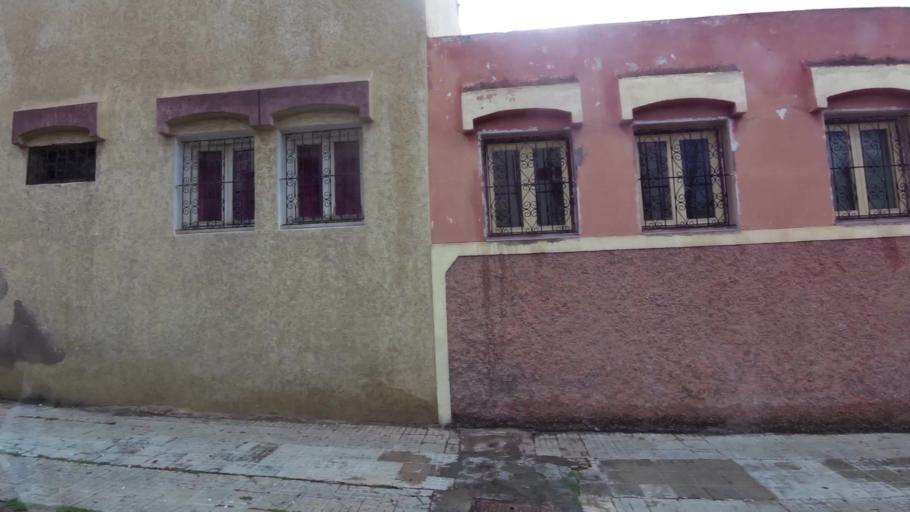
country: MA
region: Grand Casablanca
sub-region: Casablanca
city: Casablanca
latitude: 33.5649
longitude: -7.6711
